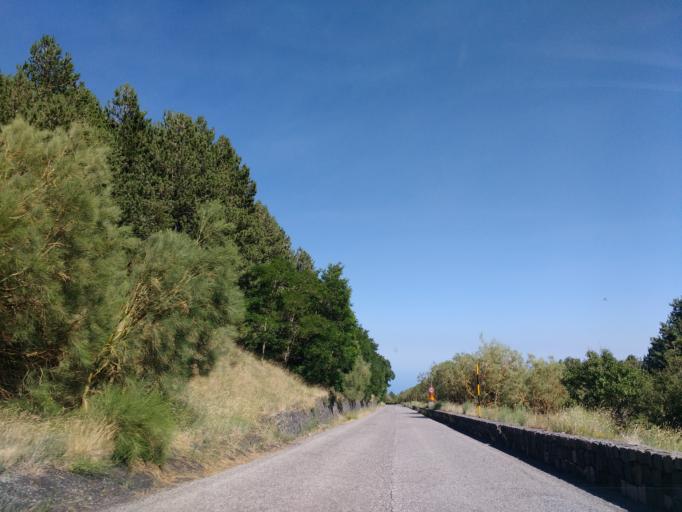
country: IT
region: Sicily
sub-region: Catania
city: Nicolosi
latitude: 37.6996
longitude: 15.0168
